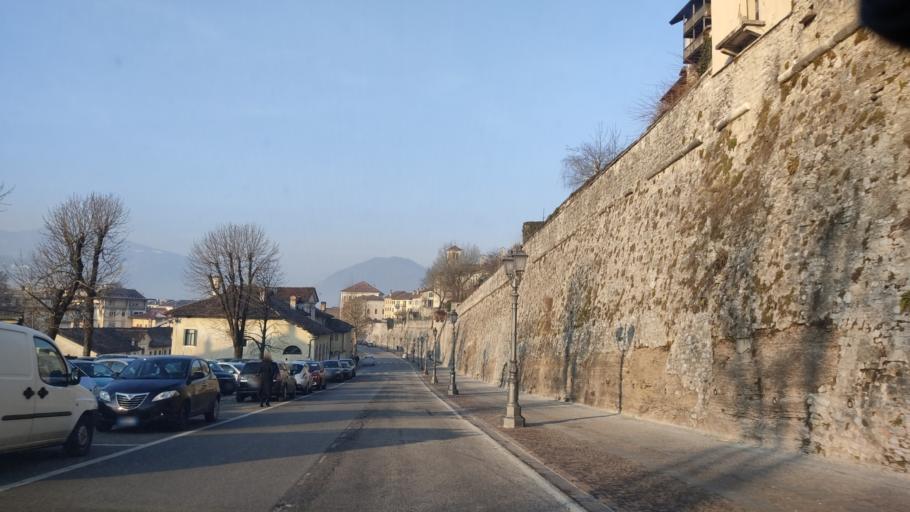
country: IT
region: Veneto
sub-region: Provincia di Belluno
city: Feltre
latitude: 46.0173
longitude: 11.9098
